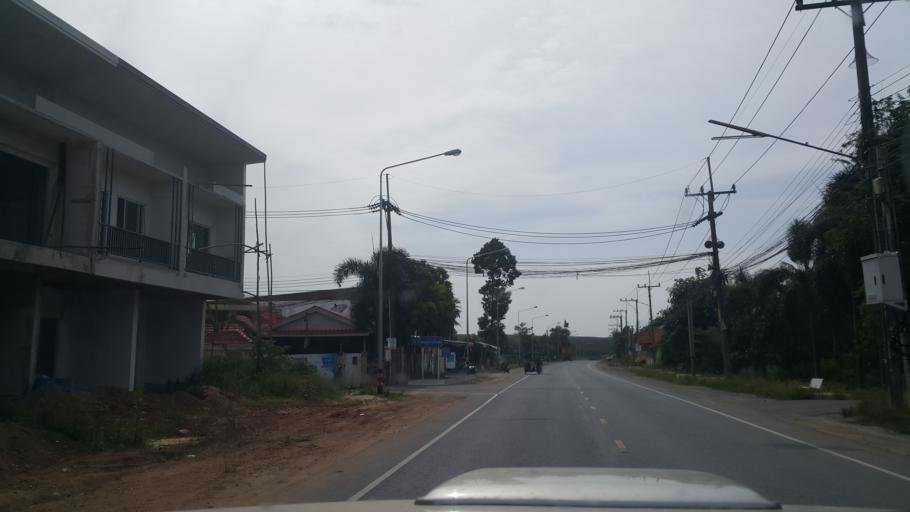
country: TH
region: Rayong
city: Ban Chang
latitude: 12.7647
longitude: 101.0172
